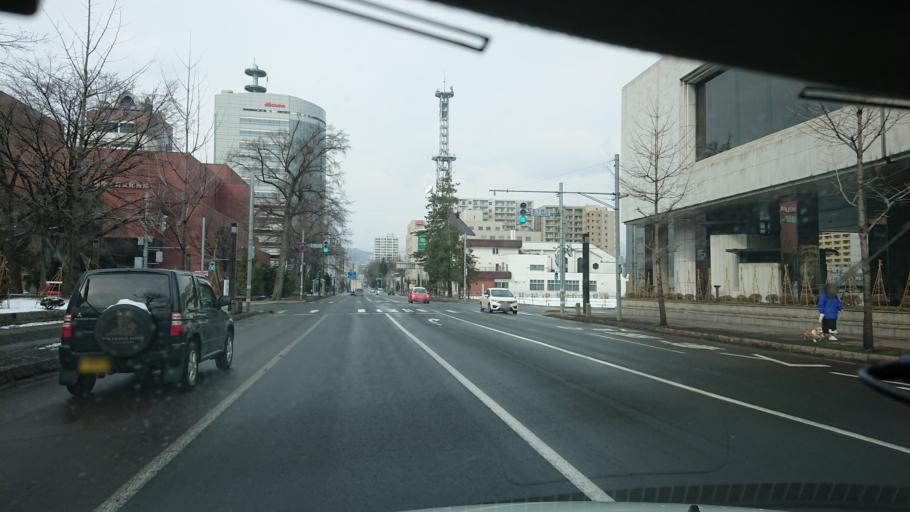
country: JP
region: Hokkaido
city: Sapporo
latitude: 43.0603
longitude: 141.3364
